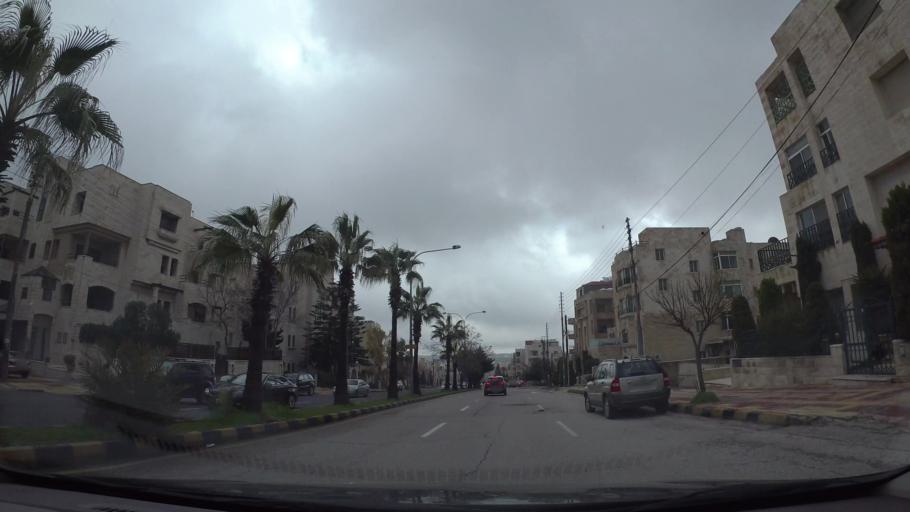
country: JO
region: Amman
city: Wadi as Sir
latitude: 31.9480
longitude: 35.8701
